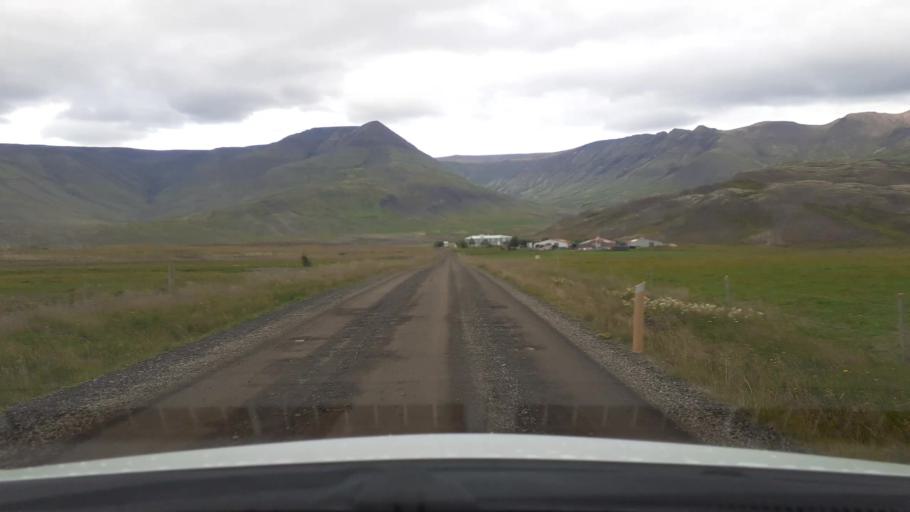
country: IS
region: Capital Region
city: Mosfellsbaer
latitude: 64.2009
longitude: -21.5590
